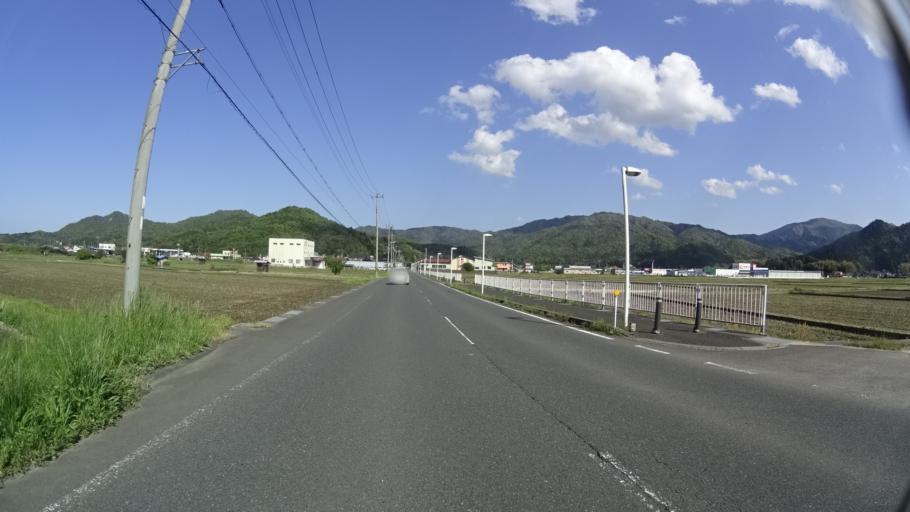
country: JP
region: Kyoto
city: Miyazu
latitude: 35.5330
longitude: 135.1173
